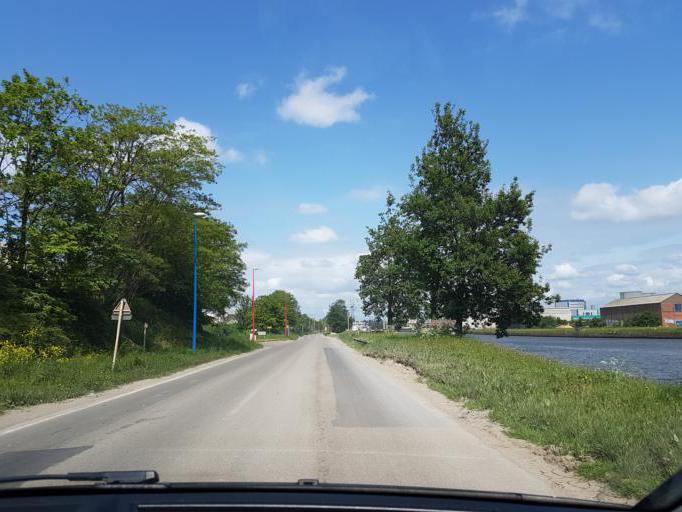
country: BE
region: Flanders
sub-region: Provincie Vlaams-Brabant
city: Vilvoorde
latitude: 50.9334
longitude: 4.4120
